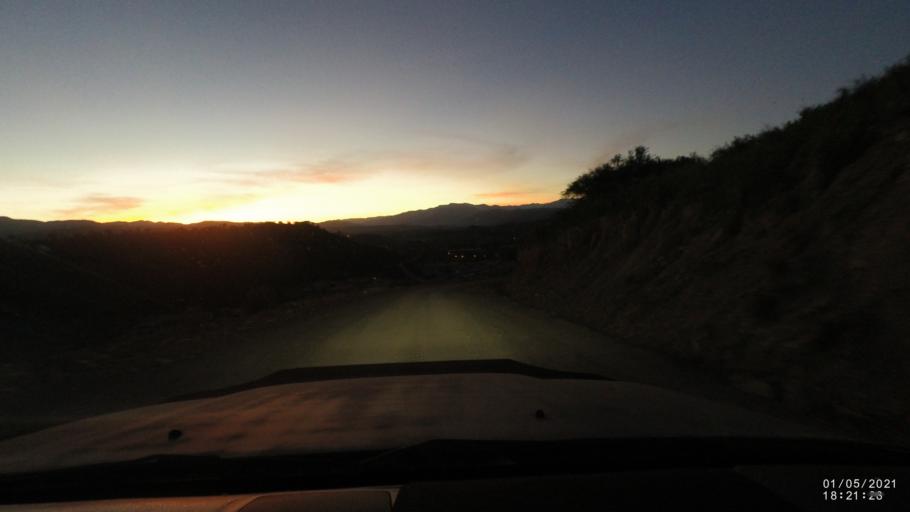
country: BO
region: Cochabamba
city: Capinota
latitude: -17.6625
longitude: -66.2302
